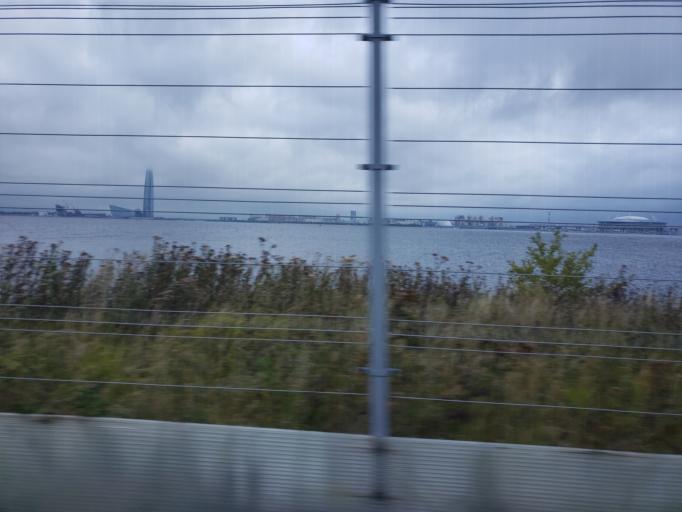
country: RU
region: St.-Petersburg
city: Lakhtinskiy
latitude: 59.9534
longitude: 30.1868
